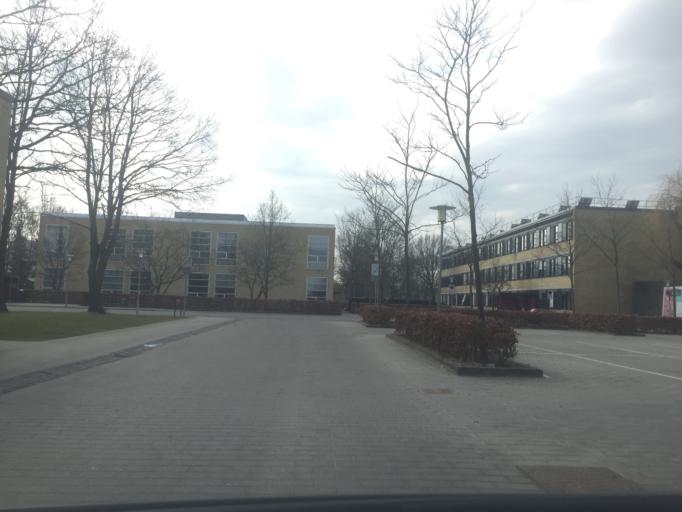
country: DK
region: Capital Region
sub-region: Lyngby-Tarbaek Kommune
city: Kongens Lyngby
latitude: 55.7803
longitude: 12.5208
